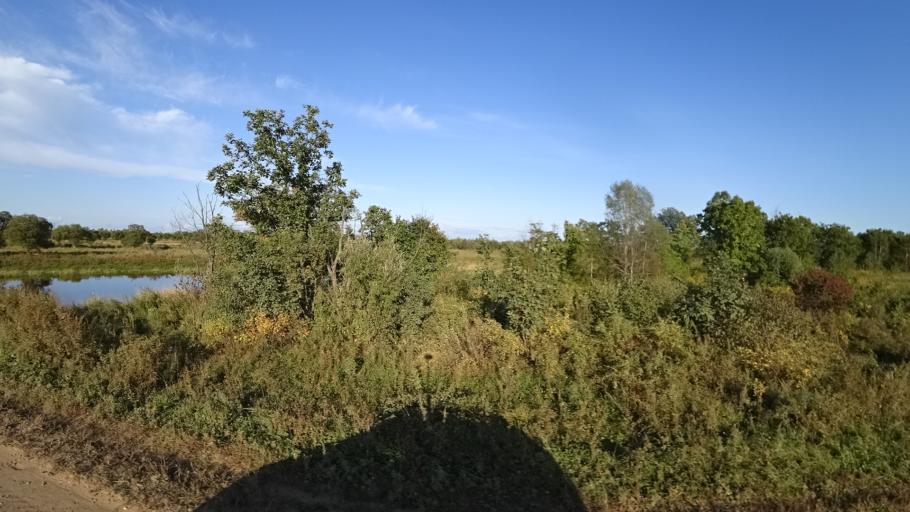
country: RU
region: Amur
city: Arkhara
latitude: 49.3601
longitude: 130.1369
